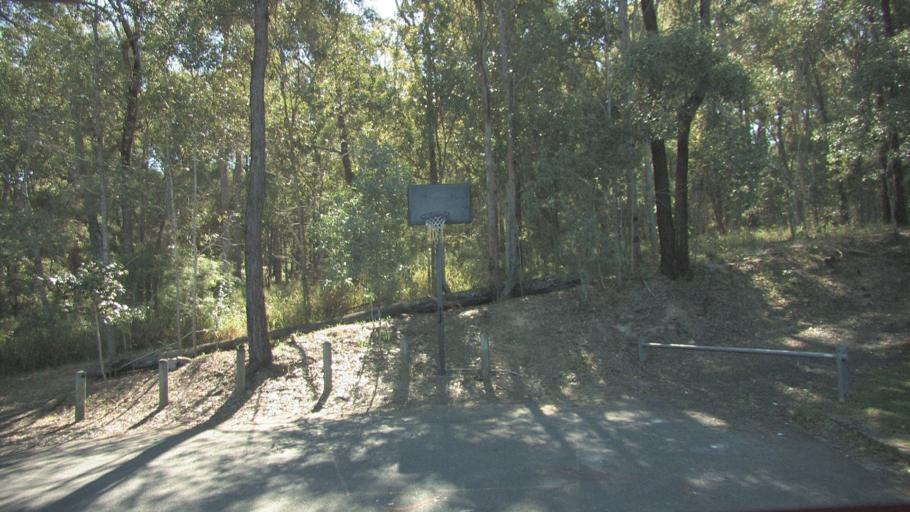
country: AU
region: Queensland
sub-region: Logan
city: Slacks Creek
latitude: -27.6387
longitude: 153.1723
